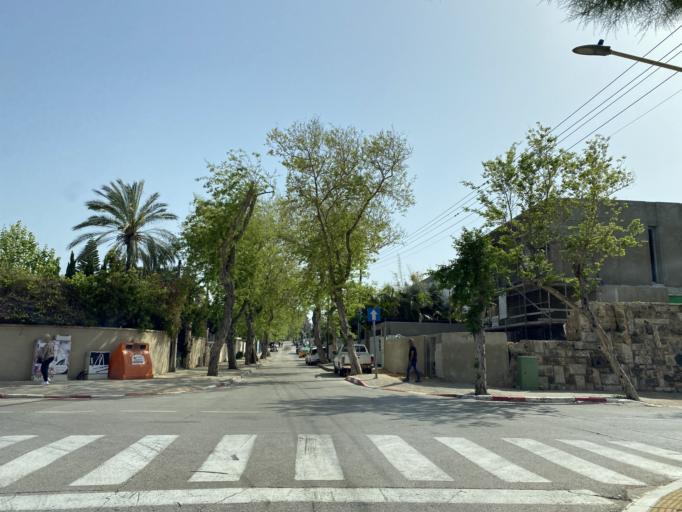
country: IL
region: Tel Aviv
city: Herzliya Pituah
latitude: 32.1784
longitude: 34.8080
